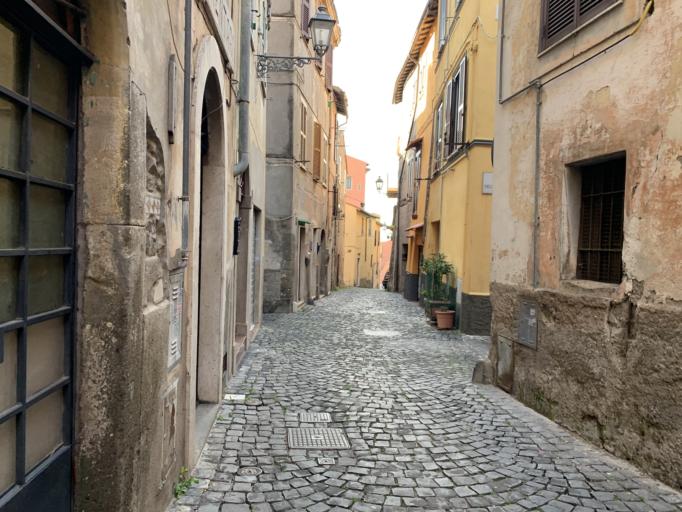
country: IT
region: Latium
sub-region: Citta metropolitana di Roma Capitale
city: Castel Gandolfo
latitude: 41.7692
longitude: 12.6598
